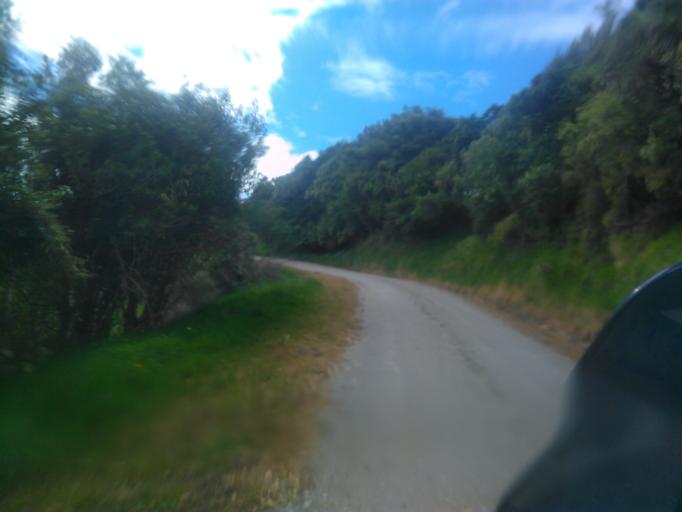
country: NZ
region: Hawke's Bay
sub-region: Wairoa District
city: Wairoa
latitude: -38.7710
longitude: 177.6389
